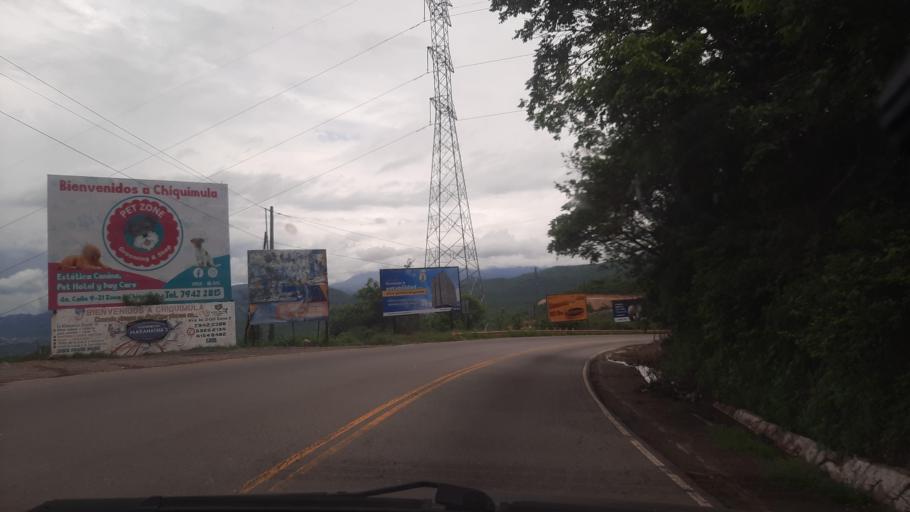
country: GT
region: Chiquimula
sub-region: Municipio de Chiquimula
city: Chiquimula
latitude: 14.8625
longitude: -89.5102
